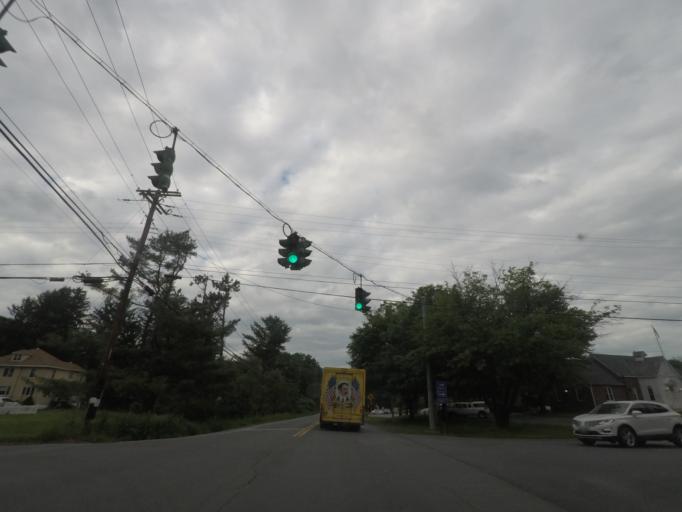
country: US
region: New York
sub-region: Orange County
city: Gardnertown
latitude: 41.5315
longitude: -74.0648
